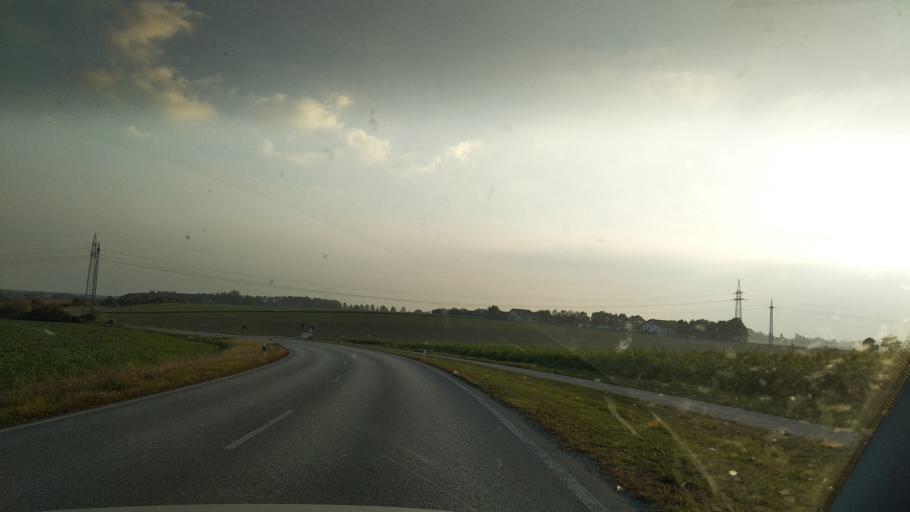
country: DE
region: Bavaria
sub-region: Upper Bavaria
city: Markt Schwaben
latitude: 48.1796
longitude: 11.8646
